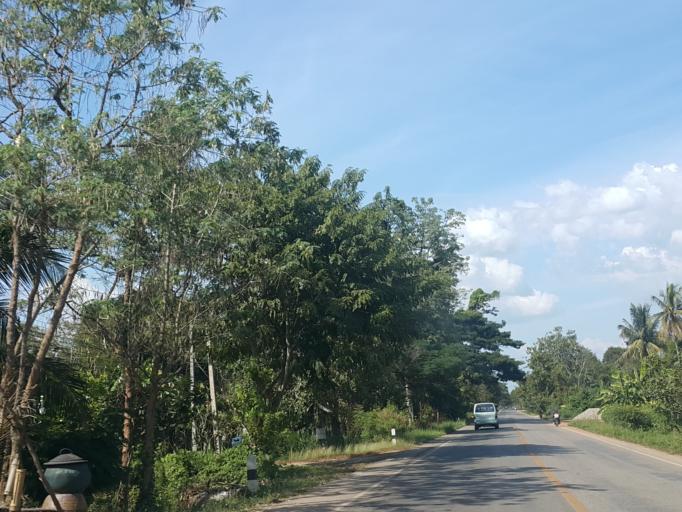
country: TH
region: Sukhothai
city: Sawankhalok
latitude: 17.2698
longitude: 99.8311
